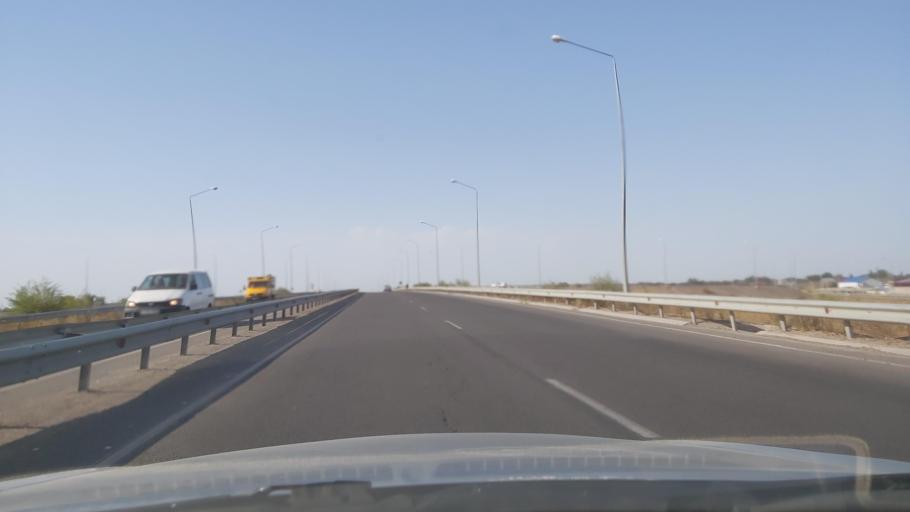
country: KZ
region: Almaty Oblysy
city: Energeticheskiy
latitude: 43.4679
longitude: 77.0325
